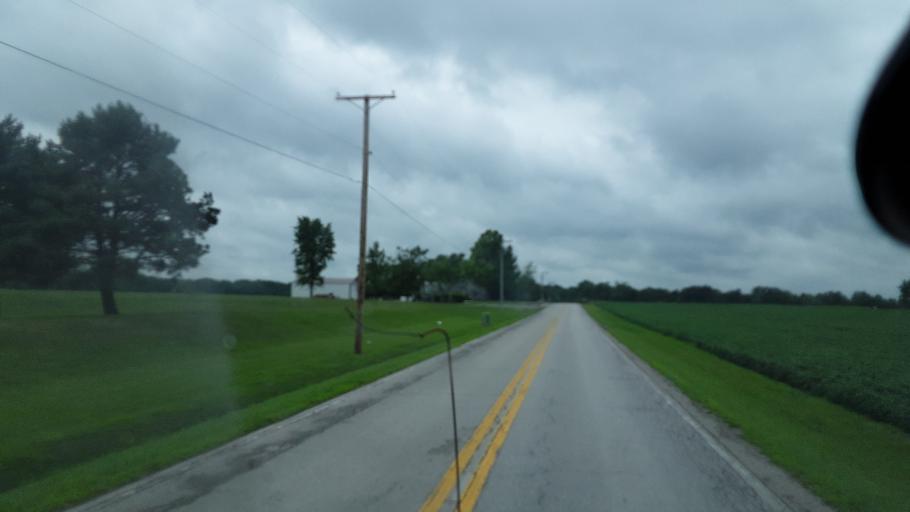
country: US
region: Indiana
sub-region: Wells County
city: Ossian
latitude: 40.9414
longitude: -85.0754
